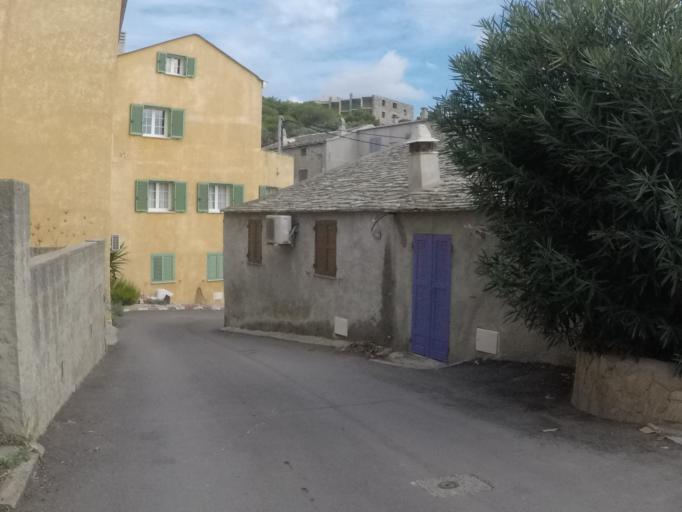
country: FR
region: Corsica
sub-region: Departement de la Haute-Corse
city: Brando
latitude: 42.9661
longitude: 9.3513
